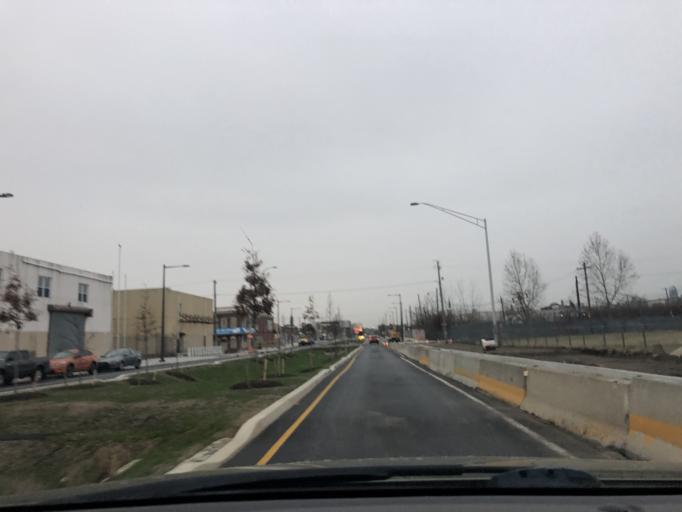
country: US
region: Pennsylvania
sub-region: Philadelphia County
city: Philadelphia
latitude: 39.9817
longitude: -75.1383
